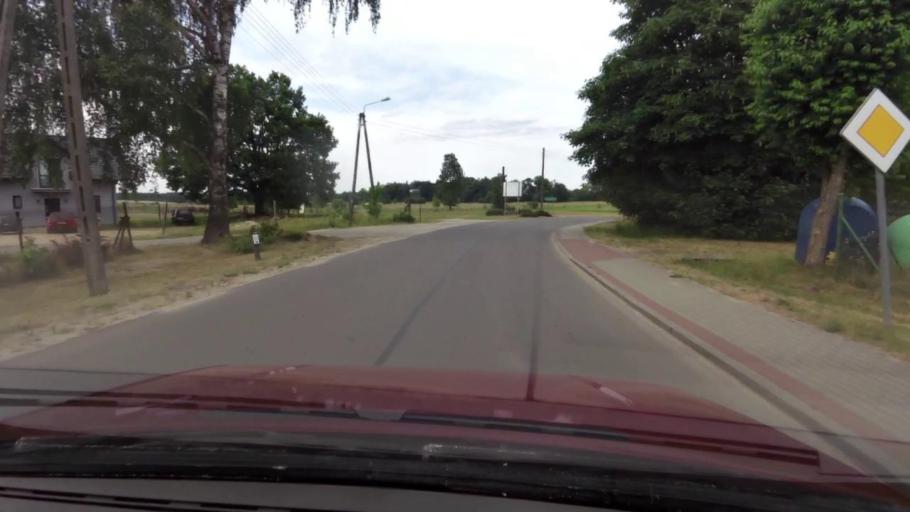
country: PL
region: Pomeranian Voivodeship
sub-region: Powiat bytowski
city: Trzebielino
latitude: 54.2012
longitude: 17.0815
